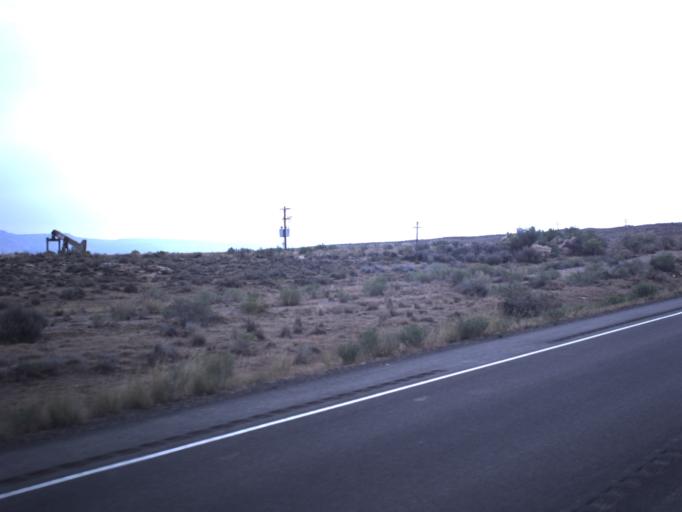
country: US
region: Utah
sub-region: Uintah County
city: Naples
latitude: 40.2111
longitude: -109.3736
